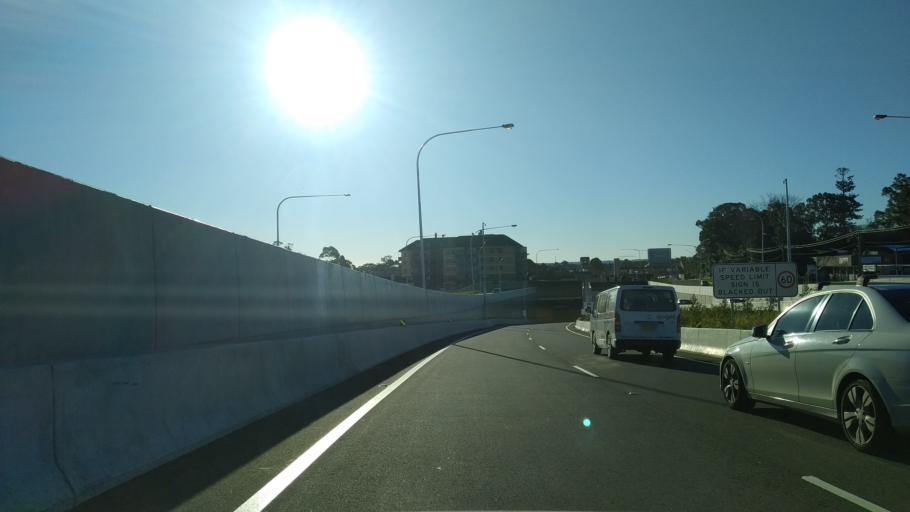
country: AU
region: New South Wales
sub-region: Ashfield
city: Summer Hill
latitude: -33.8834
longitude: 151.1336
